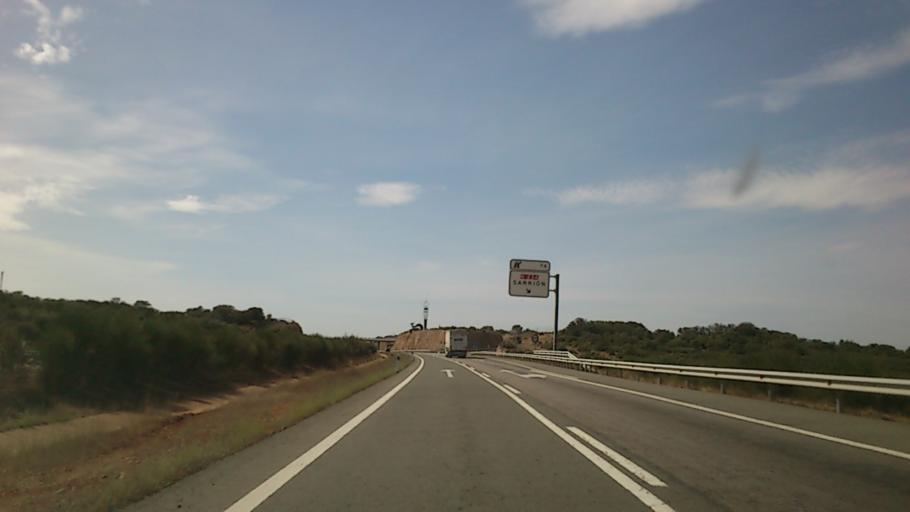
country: ES
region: Aragon
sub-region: Provincia de Teruel
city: Sarrion
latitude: 40.1448
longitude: -0.7949
